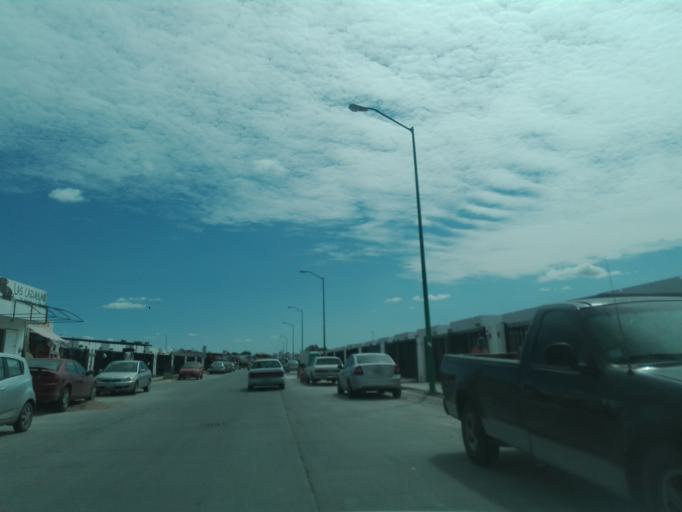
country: MX
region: Guanajuato
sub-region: Leon
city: Ladrilleras del Refugio
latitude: 21.0697
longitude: -101.5611
